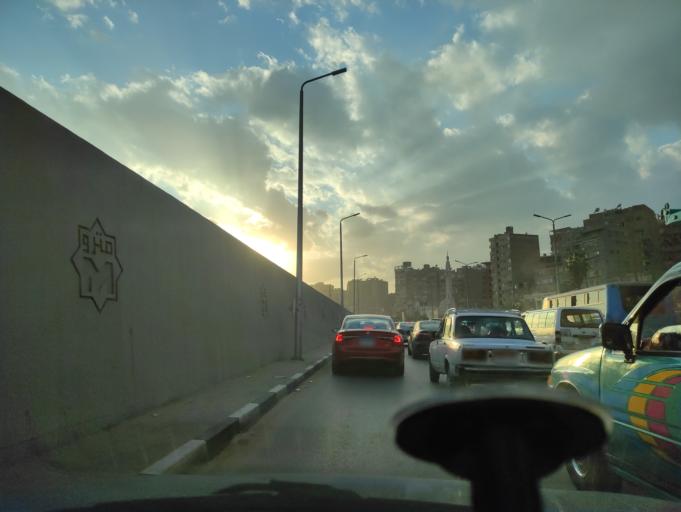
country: EG
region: Muhafazat al Qalyubiyah
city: Al Khankah
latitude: 30.1270
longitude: 31.3540
